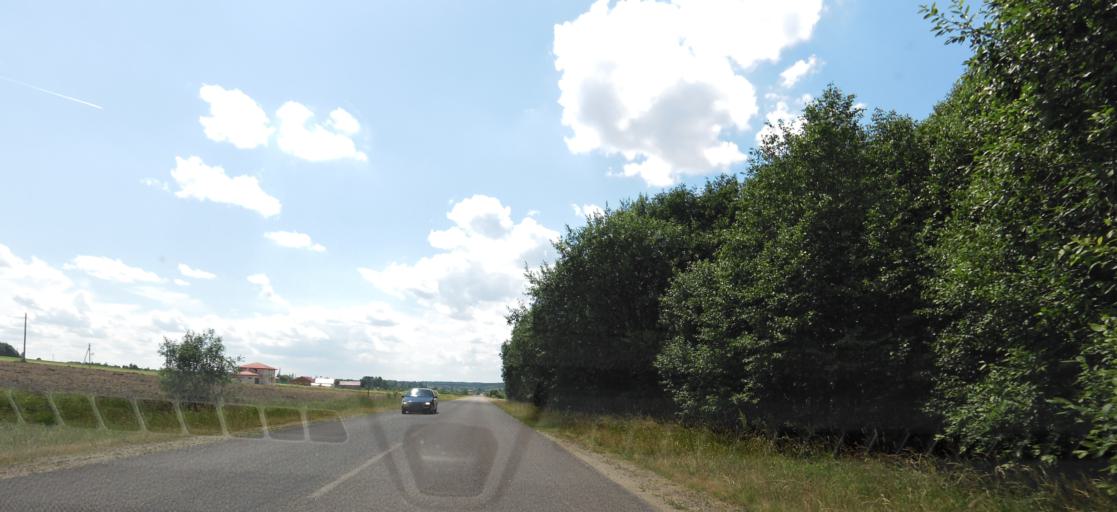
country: LT
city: Skaidiskes
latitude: 54.5561
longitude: 25.6648
